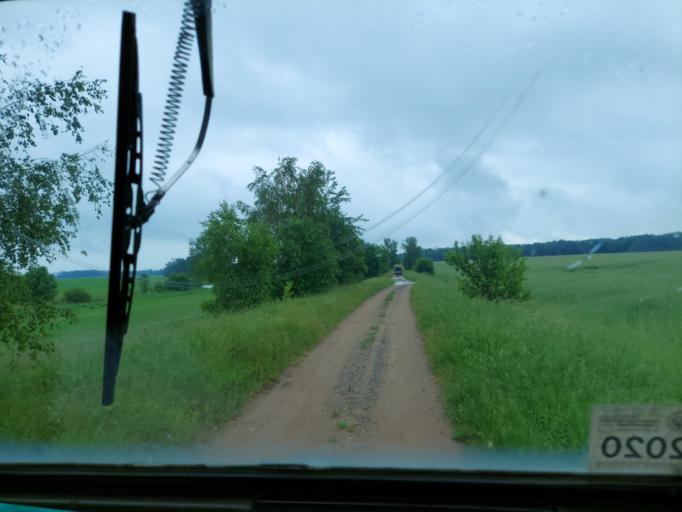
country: BY
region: Mogilev
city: Poselok Voskhod
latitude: 53.6741
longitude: 30.3928
